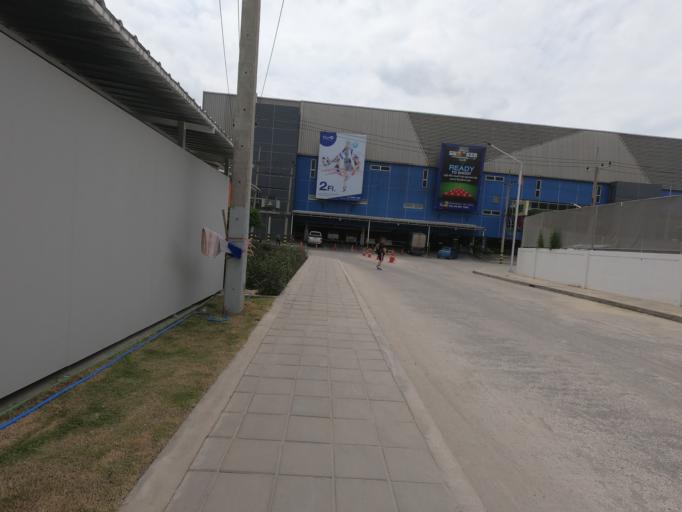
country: TH
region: Bangkok
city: Sai Mai
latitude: 13.9407
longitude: 100.6518
